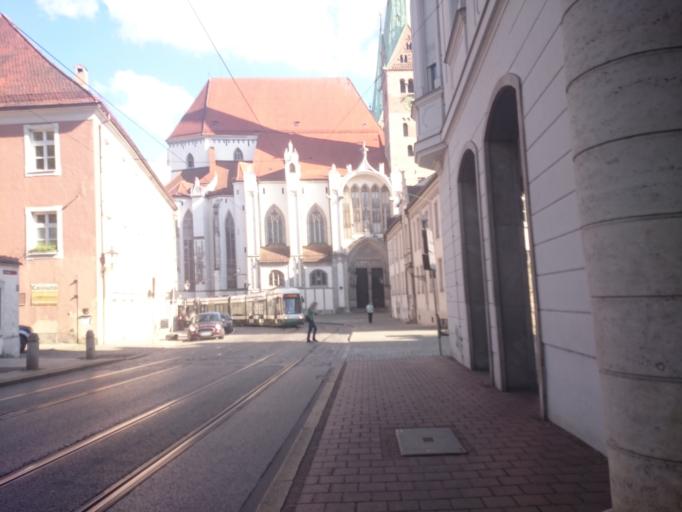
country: DE
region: Bavaria
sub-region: Swabia
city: Augsburg
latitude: 48.3737
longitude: 10.8965
